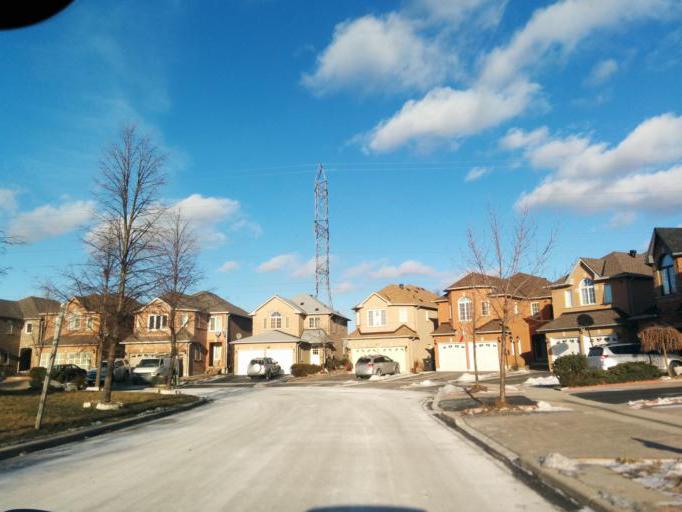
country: CA
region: Ontario
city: Mississauga
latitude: 43.6246
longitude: -79.6483
